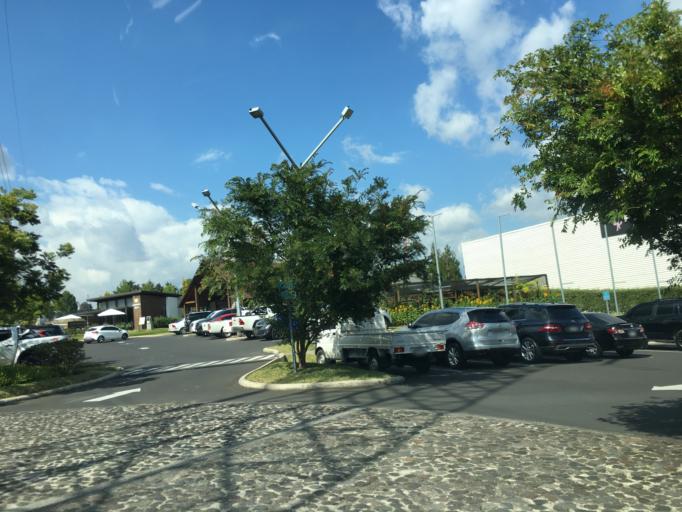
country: GT
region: Guatemala
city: Fraijanes
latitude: 14.4953
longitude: -90.4810
